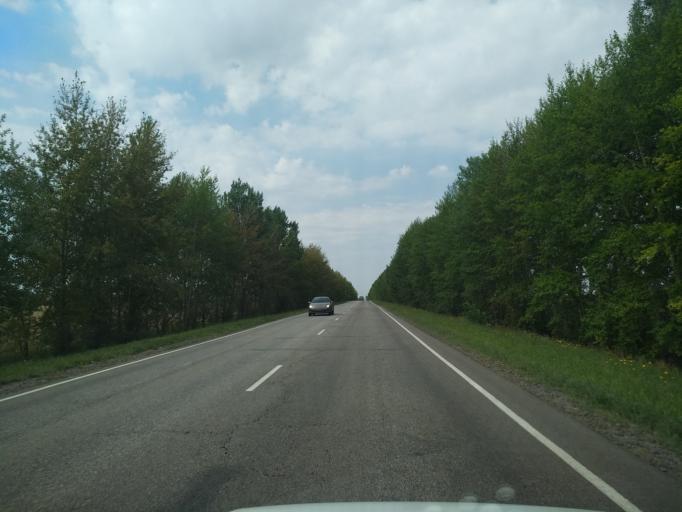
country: RU
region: Voronezj
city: Pereleshino
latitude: 51.7212
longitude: 40.0306
